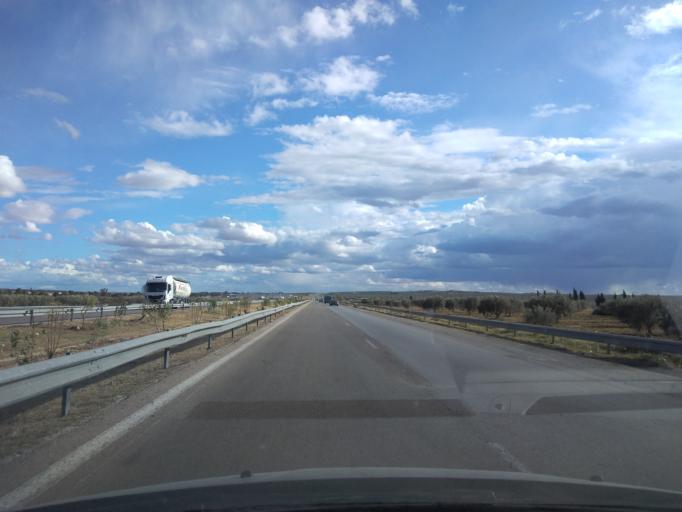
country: TN
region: Al Munastir
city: Manzil Kamil
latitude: 35.5787
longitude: 10.6093
